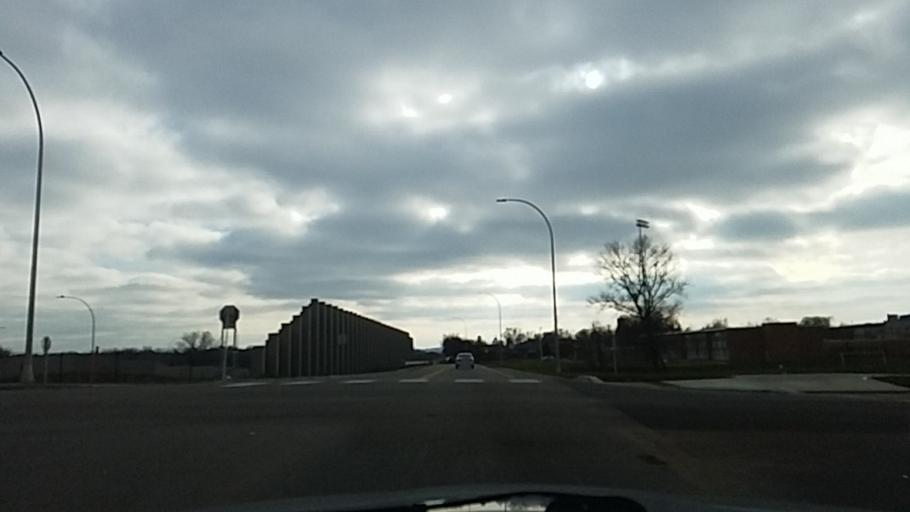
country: US
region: Minnesota
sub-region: Ramsey County
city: Little Canada
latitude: 44.9908
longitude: -93.0901
